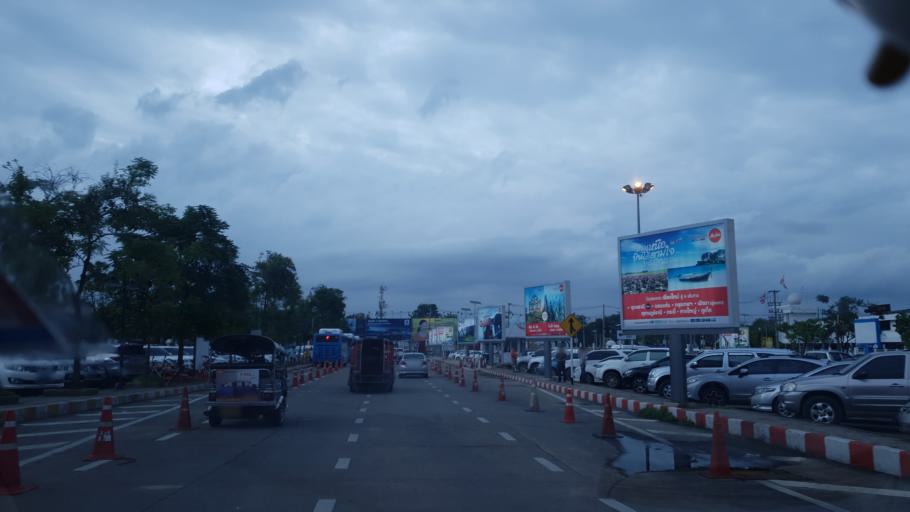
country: TH
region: Chiang Mai
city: Chiang Mai
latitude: 18.7703
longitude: 98.9685
